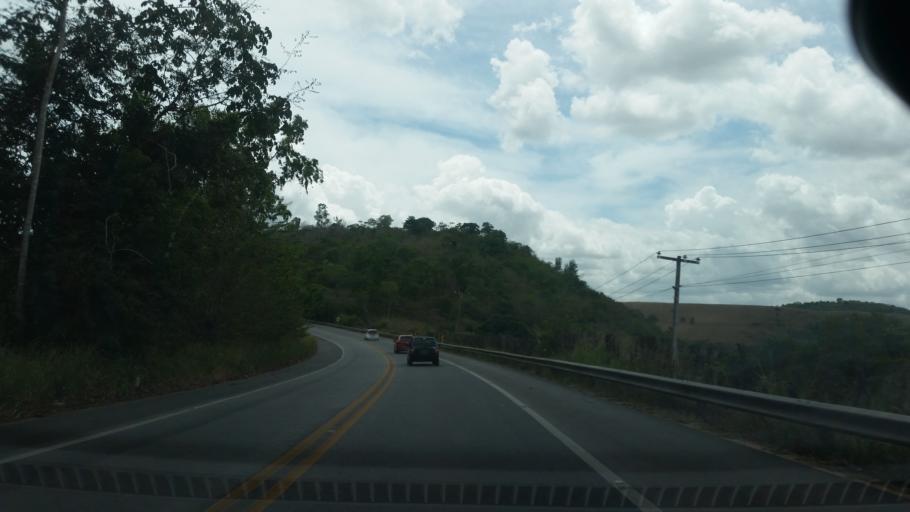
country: BR
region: Alagoas
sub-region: Uniao Dos Palmares
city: Uniao dos Palmares
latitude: -9.1909
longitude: -36.0369
